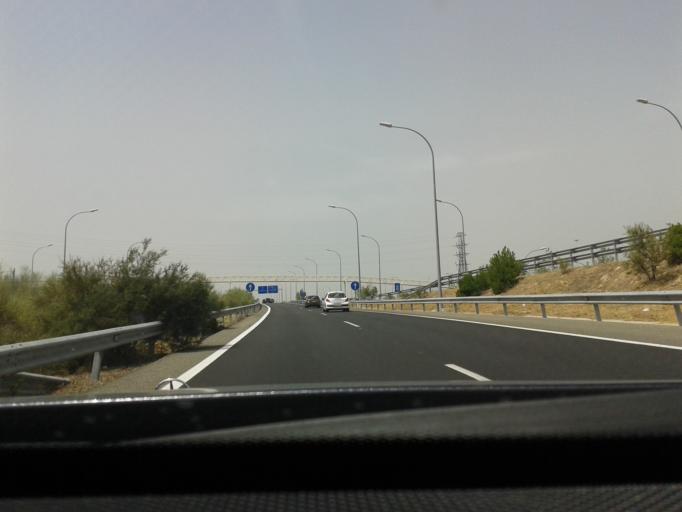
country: ES
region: Madrid
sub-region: Provincia de Madrid
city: Barajas de Madrid
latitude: 40.4800
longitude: -3.5828
